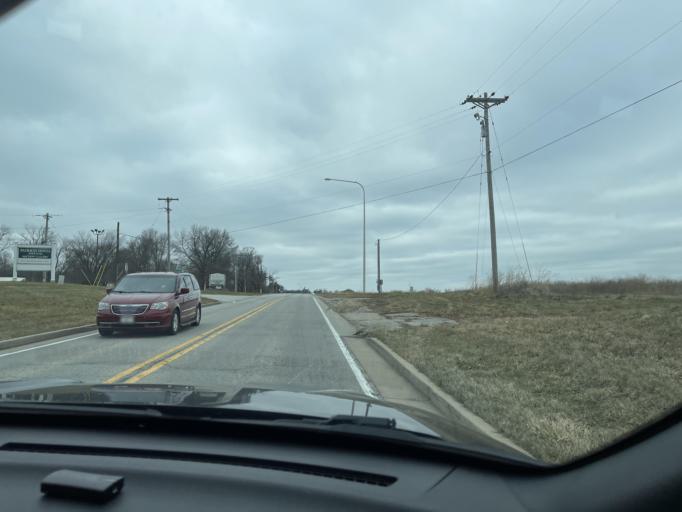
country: US
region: Illinois
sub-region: Sangamon County
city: Leland Grove
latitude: 39.8187
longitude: -89.7128
